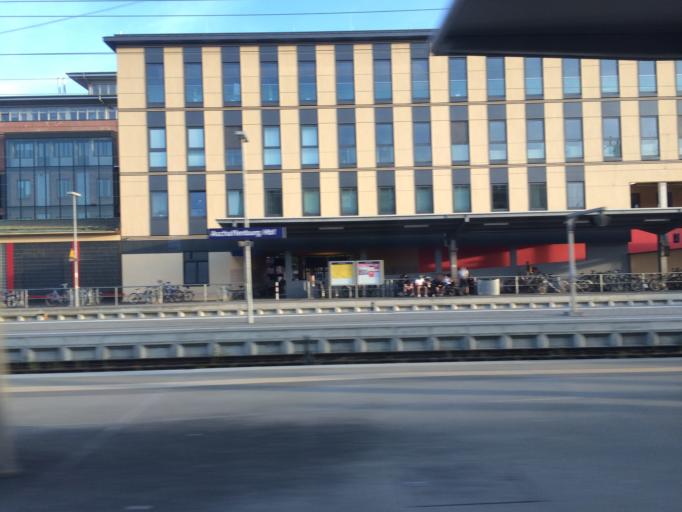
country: DE
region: Bavaria
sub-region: Regierungsbezirk Unterfranken
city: Aschaffenburg
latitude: 49.9803
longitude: 9.1444
